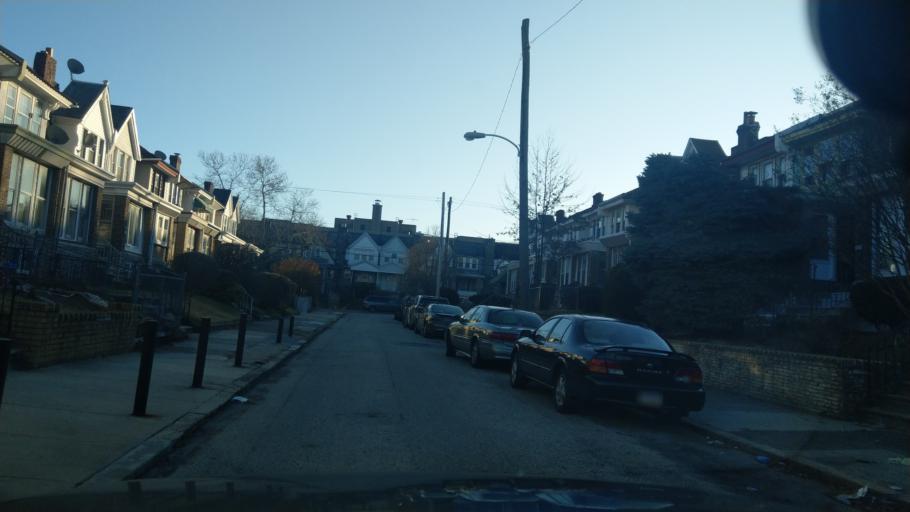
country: US
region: Pennsylvania
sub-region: Montgomery County
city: Wyncote
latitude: 40.0535
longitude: -75.1473
